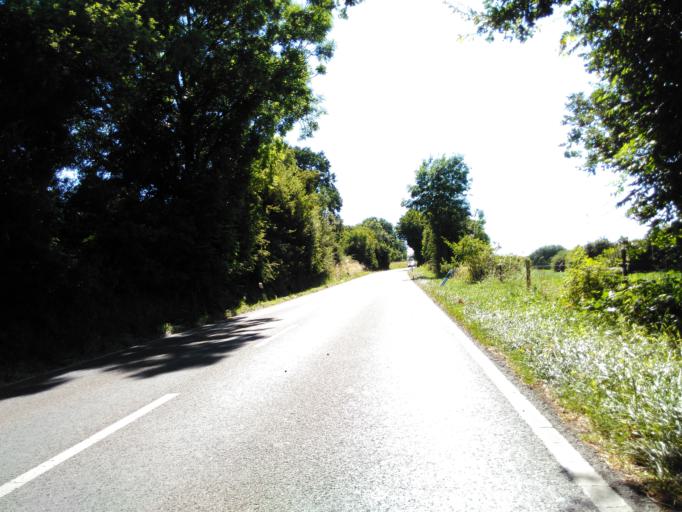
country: LU
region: Luxembourg
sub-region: Canton d'Esch-sur-Alzette
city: Reckange-sur-Mess
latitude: 49.5616
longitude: 6.0003
